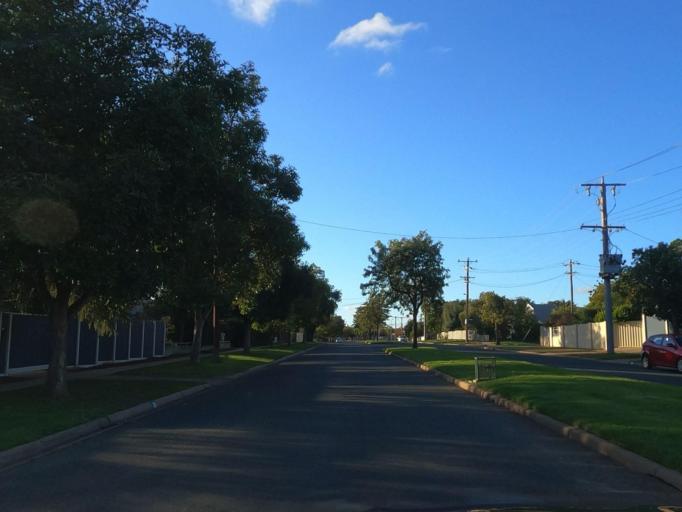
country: AU
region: Victoria
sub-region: Swan Hill
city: Swan Hill
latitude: -35.3465
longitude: 143.5556
